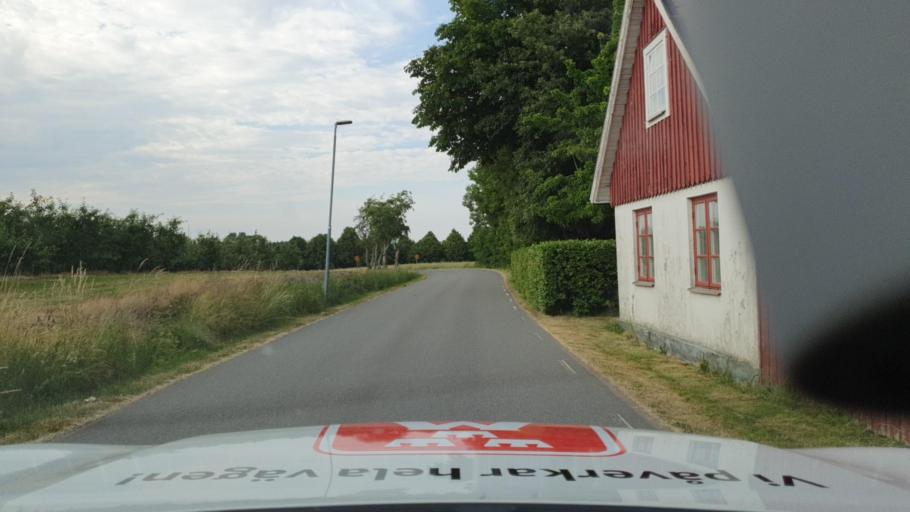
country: SE
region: Skane
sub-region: Simrishamns Kommun
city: Kivik
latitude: 55.6665
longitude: 14.2163
